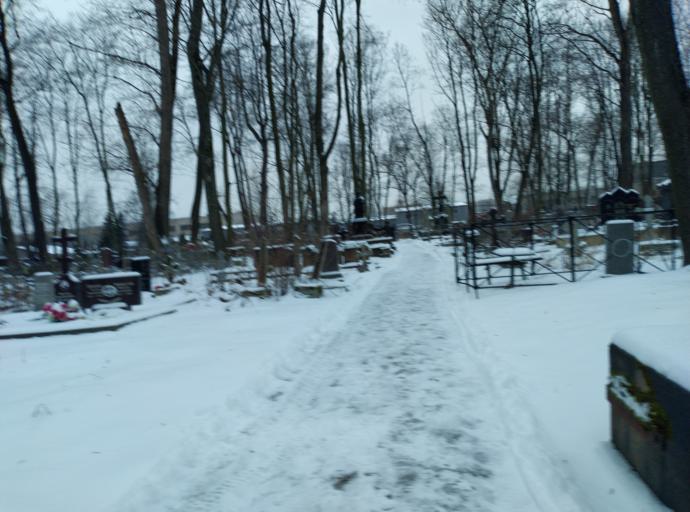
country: RU
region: St.-Petersburg
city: Centralniy
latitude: 59.9028
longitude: 30.3588
